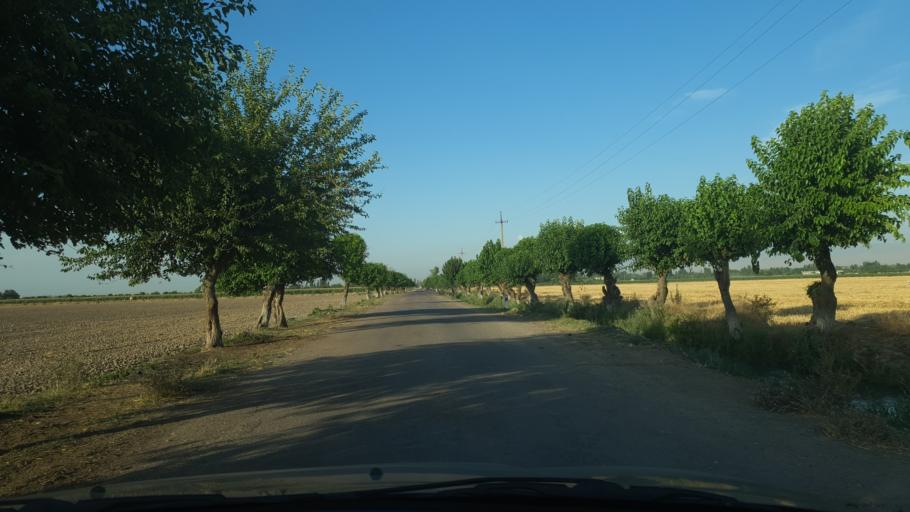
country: UZ
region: Toshkent
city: Tuytepa
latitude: 41.0993
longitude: 69.3793
